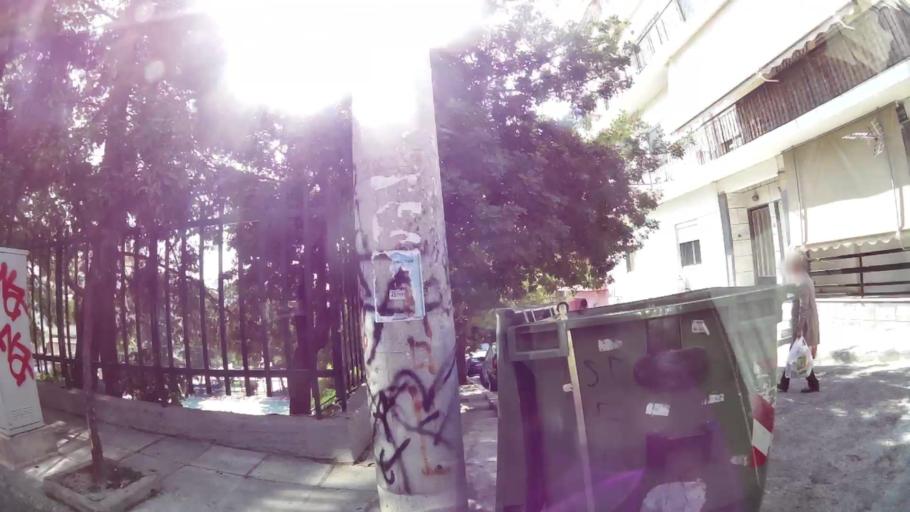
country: GR
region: Attica
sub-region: Nomos Piraios
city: Drapetsona
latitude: 37.9520
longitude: 23.6154
